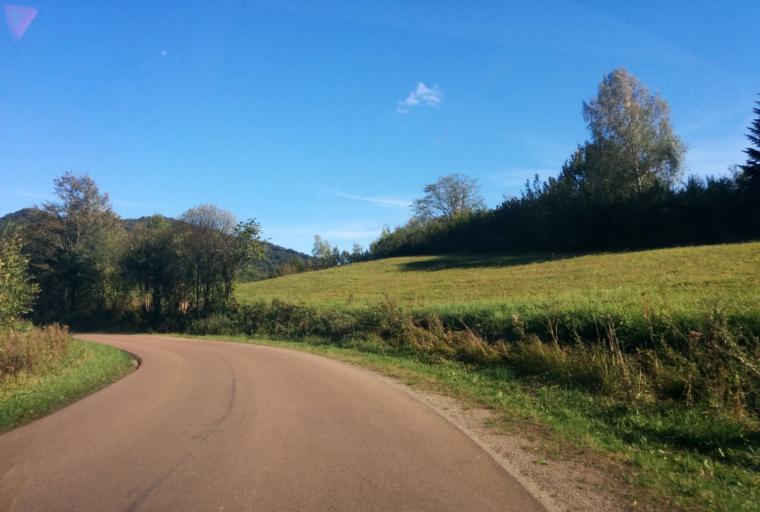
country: PL
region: Subcarpathian Voivodeship
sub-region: Powiat leski
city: Polanczyk
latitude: 49.3010
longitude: 22.4264
